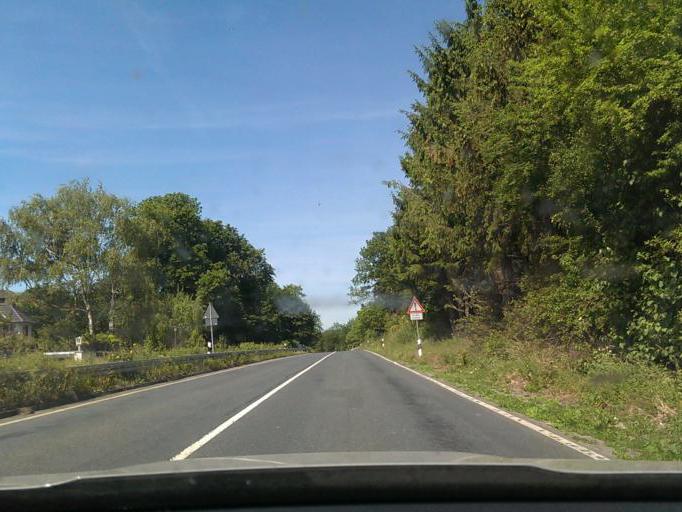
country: DE
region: Lower Saxony
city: Elze
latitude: 52.1236
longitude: 9.7364
